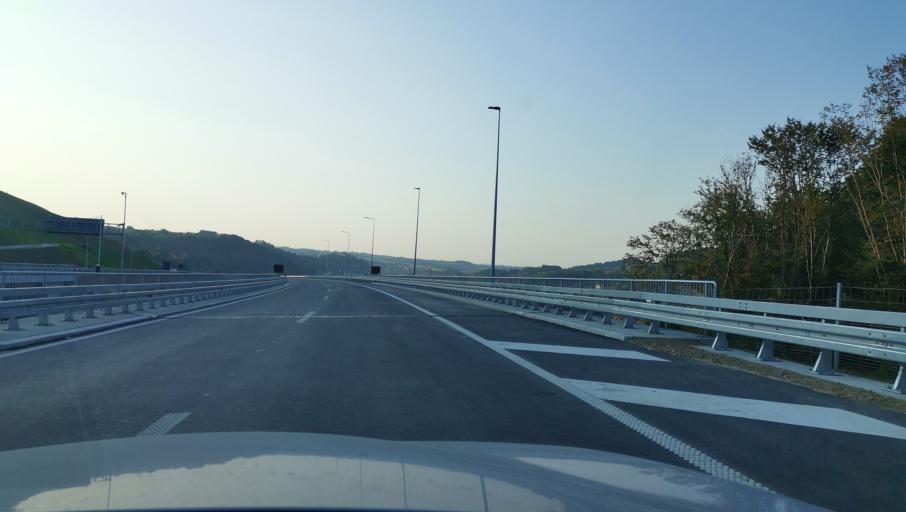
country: RS
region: Central Serbia
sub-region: Kolubarski Okrug
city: Ljig
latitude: 44.2118
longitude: 20.2629
